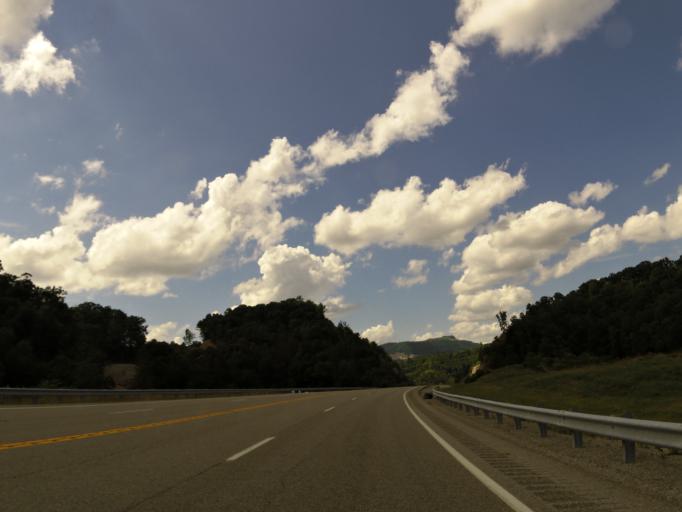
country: US
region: Virginia
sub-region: Lee County
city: Jonesville
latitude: 36.7639
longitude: -83.2012
